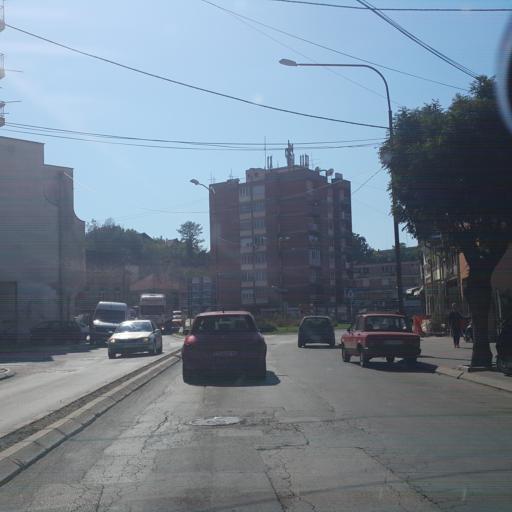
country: RS
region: Central Serbia
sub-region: Zajecarski Okrug
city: Knjazevac
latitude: 43.5681
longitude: 22.2589
